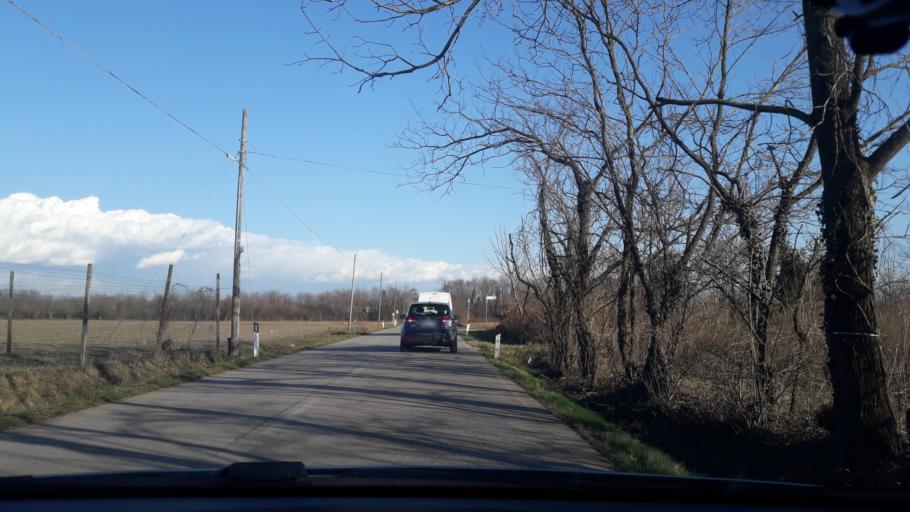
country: IT
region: Friuli Venezia Giulia
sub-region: Provincia di Udine
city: Passons
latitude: 46.0742
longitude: 13.1731
